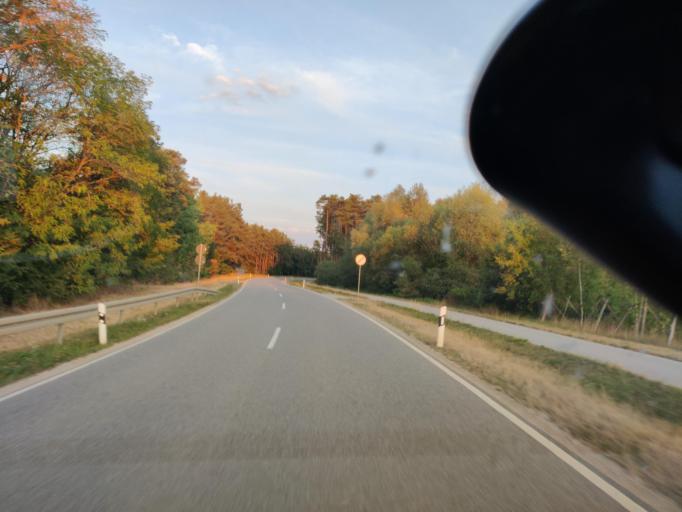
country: DE
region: Bavaria
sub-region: Regierungsbezirk Mittelfranken
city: Hilpoltstein
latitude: 49.1591
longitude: 11.2002
